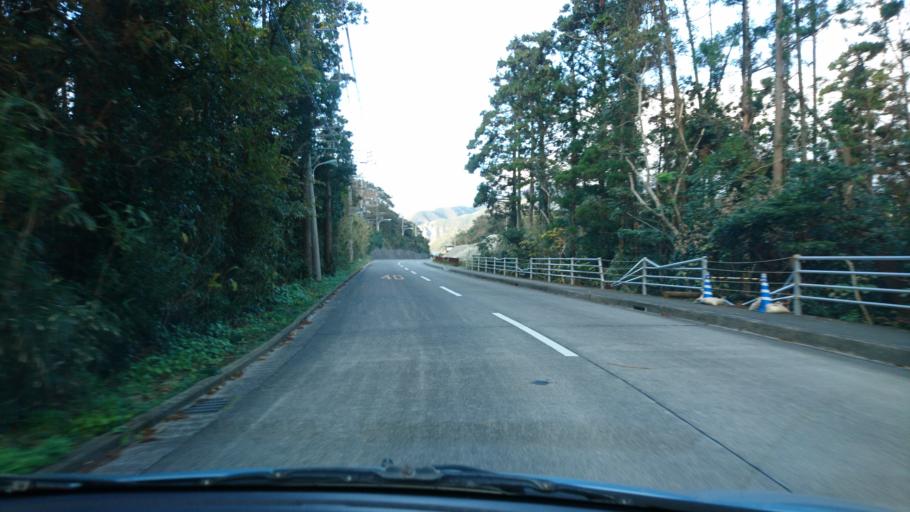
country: JP
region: Shizuoka
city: Shimoda
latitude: 34.3653
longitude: 139.2587
